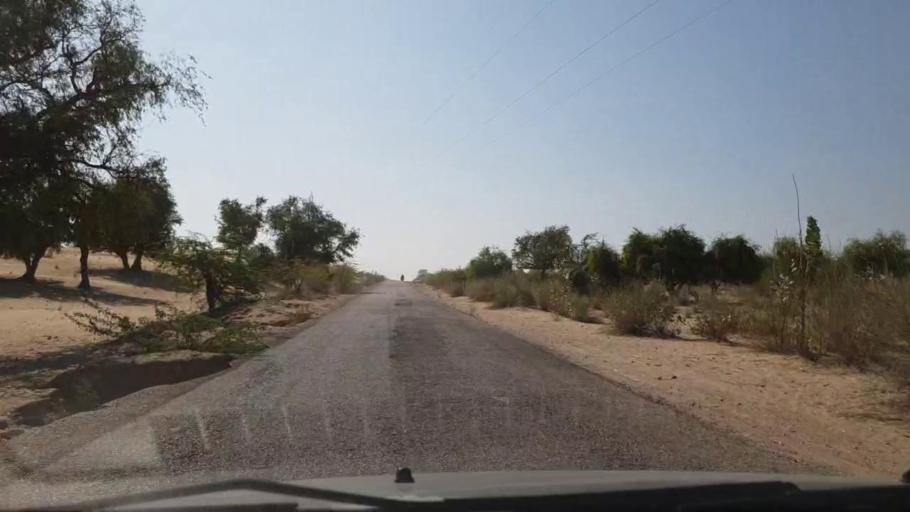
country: PK
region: Sindh
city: Mithi
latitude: 24.5869
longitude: 69.7071
